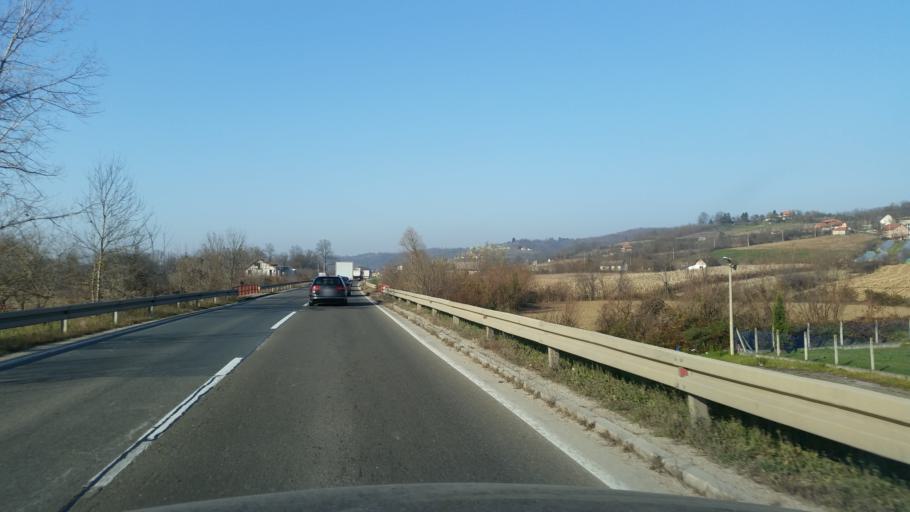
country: RS
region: Central Serbia
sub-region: Belgrade
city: Lazarevac
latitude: 44.3232
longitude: 20.2245
